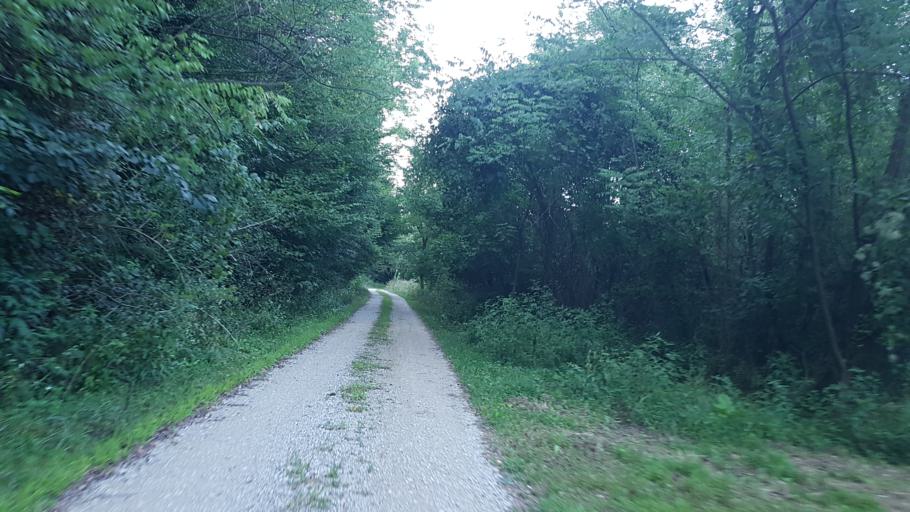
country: IT
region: Friuli Venezia Giulia
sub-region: Provincia di Gorizia
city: Mossa
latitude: 45.9435
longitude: 13.5362
